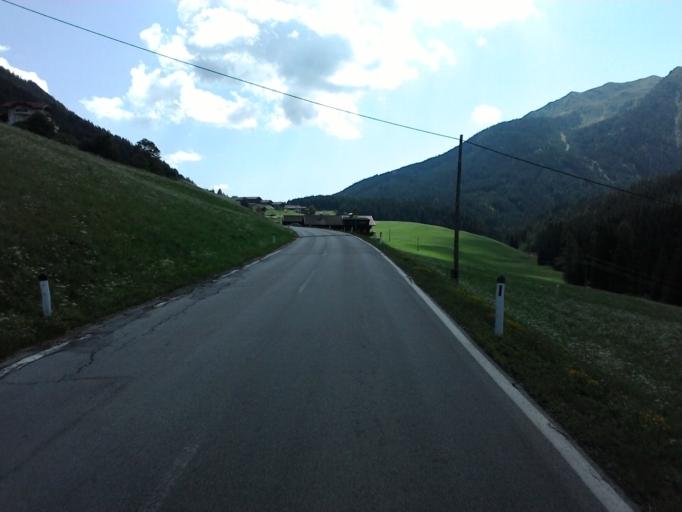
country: AT
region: Tyrol
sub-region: Politischer Bezirk Lienz
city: Kartitsch
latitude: 46.7225
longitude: 12.5117
